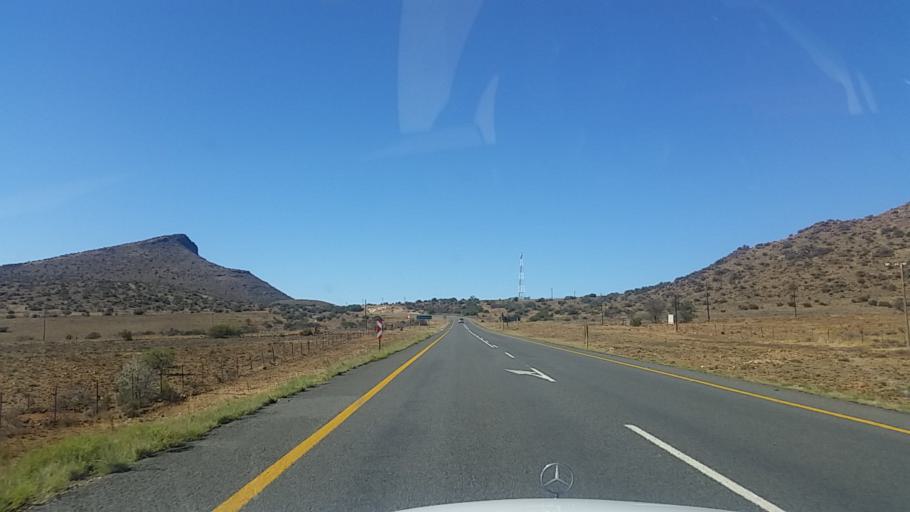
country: ZA
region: Eastern Cape
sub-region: Cacadu District Municipality
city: Graaff-Reinet
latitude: -32.1022
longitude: 24.6057
